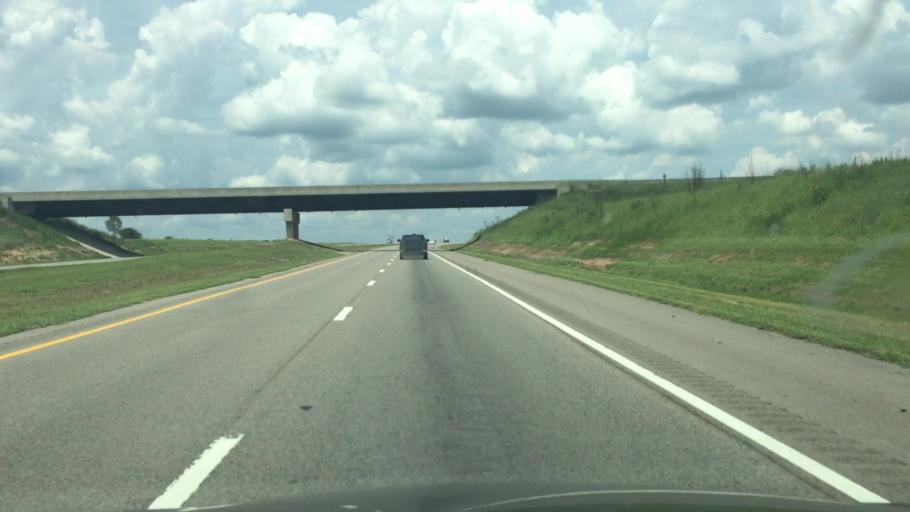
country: US
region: North Carolina
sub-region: Richmond County
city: Ellerbe
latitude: 35.1863
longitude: -79.7209
